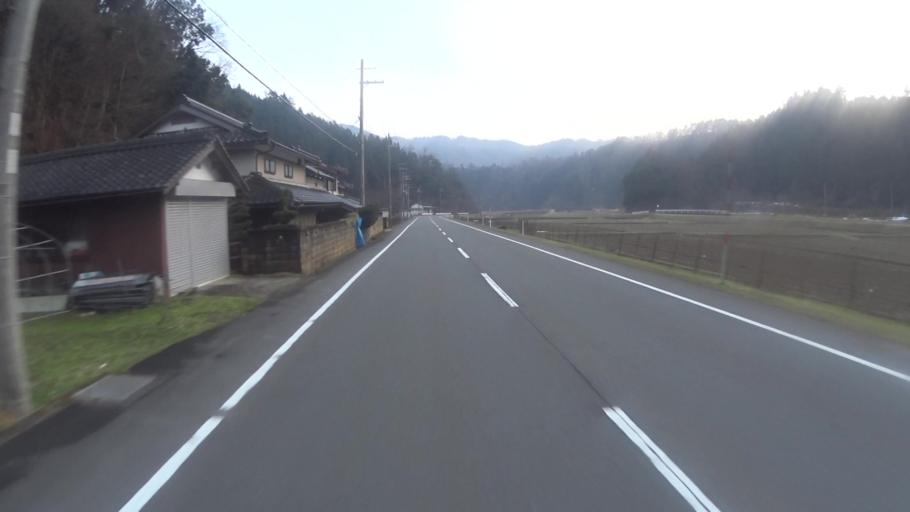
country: JP
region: Kyoto
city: Maizuru
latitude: 35.3976
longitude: 135.4626
